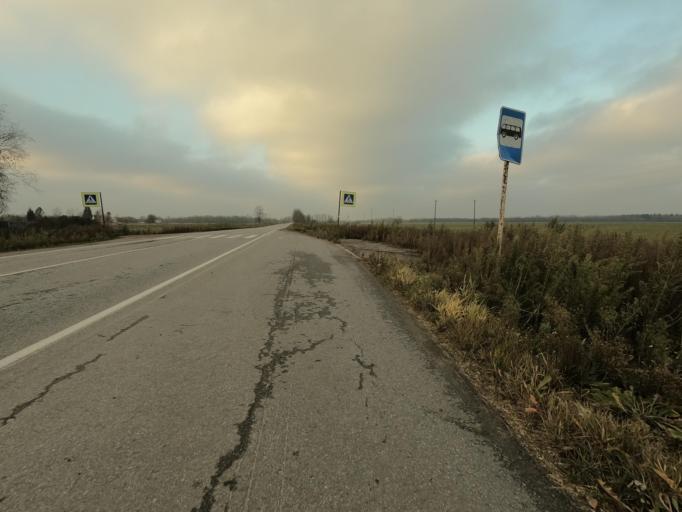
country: RU
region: Leningrad
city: Mga
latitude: 59.7546
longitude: 31.0367
